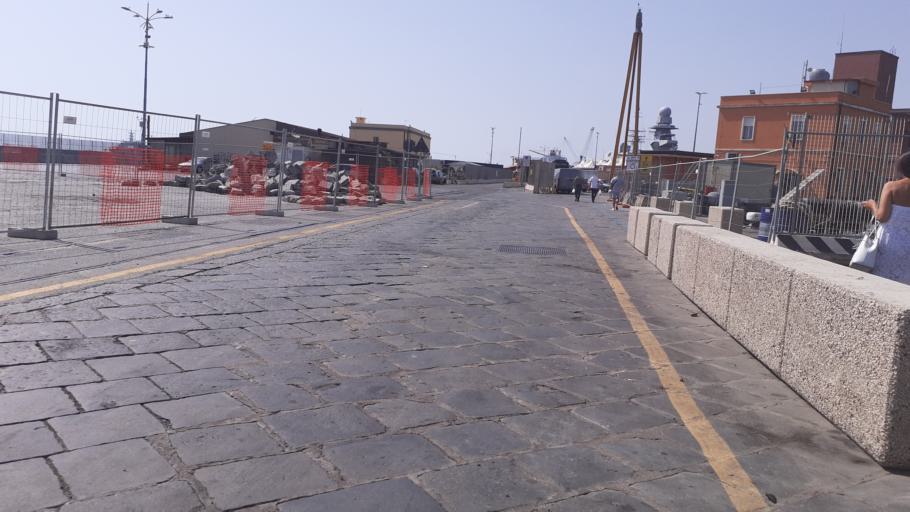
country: IT
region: Sicily
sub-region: Catania
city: Catania
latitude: 37.4992
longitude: 15.0945
